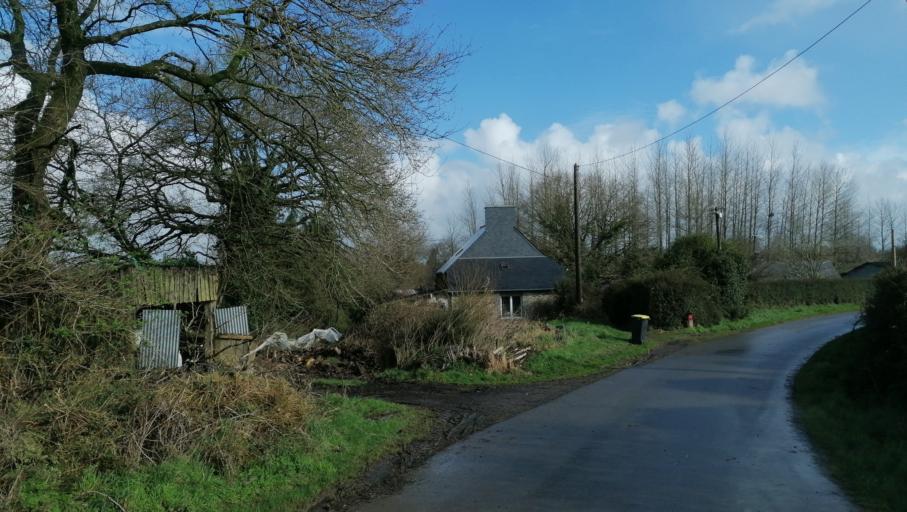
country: FR
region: Brittany
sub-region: Departement des Cotes-d'Armor
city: Lanrodec
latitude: 48.4956
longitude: -3.0235
